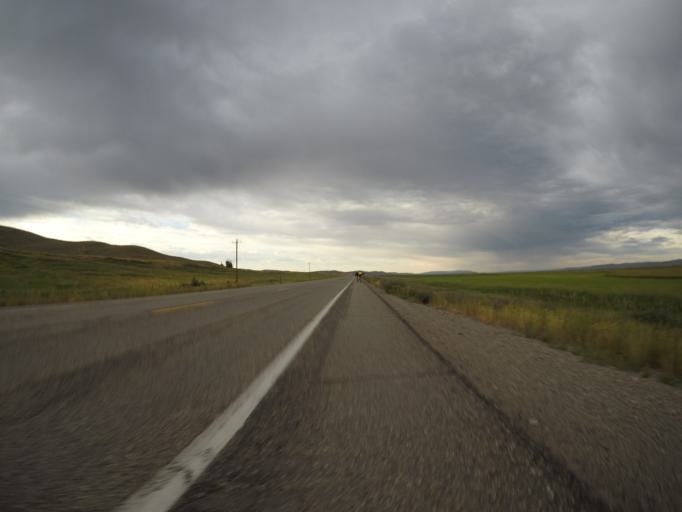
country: US
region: Utah
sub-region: Rich County
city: Randolph
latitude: 41.9648
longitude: -110.9479
